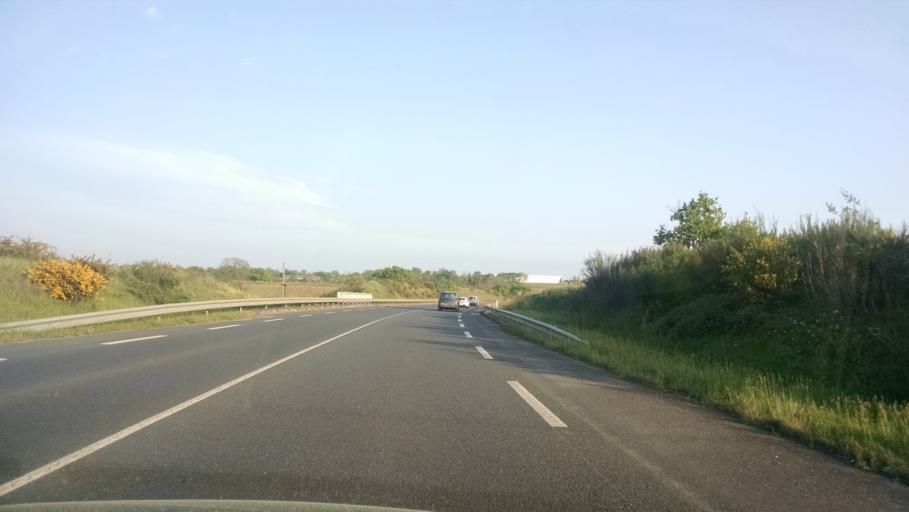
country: FR
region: Pays de la Loire
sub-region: Departement de la Loire-Atlantique
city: Clisson
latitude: 47.0941
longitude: -1.2665
